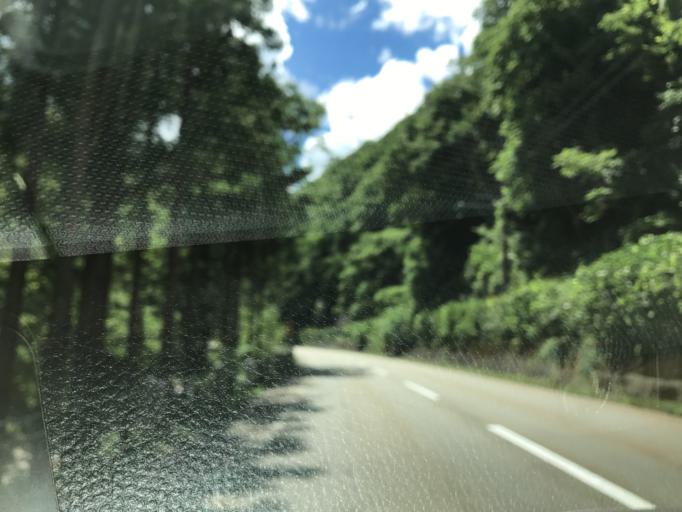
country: JP
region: Gifu
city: Takayama
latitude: 36.0976
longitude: 137.1106
